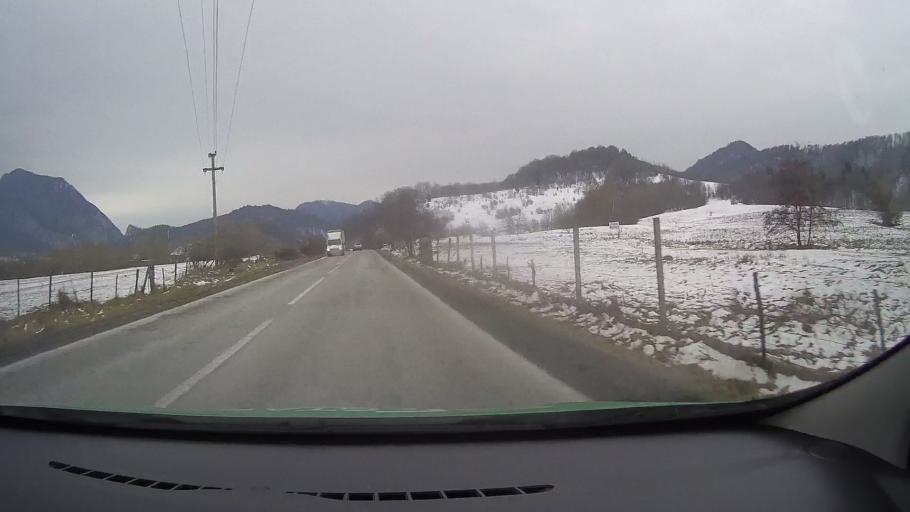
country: RO
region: Brasov
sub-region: Oras Rasnov
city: Rasnov
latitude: 45.5516
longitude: 25.4894
